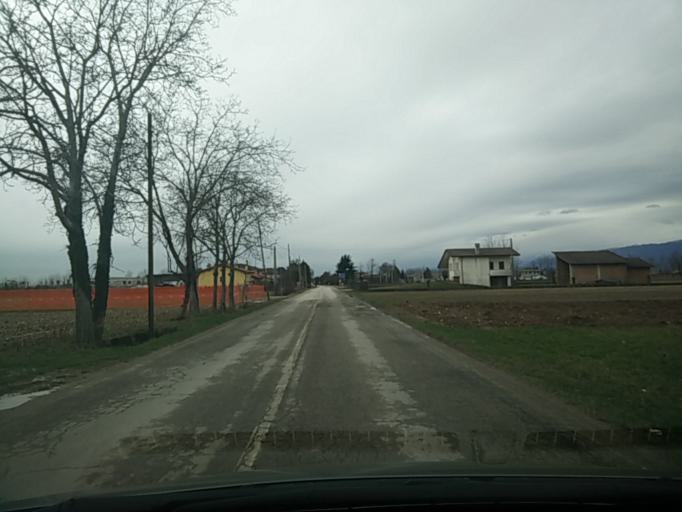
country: IT
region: Veneto
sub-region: Provincia di Treviso
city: San Vito
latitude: 45.7635
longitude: 11.9104
